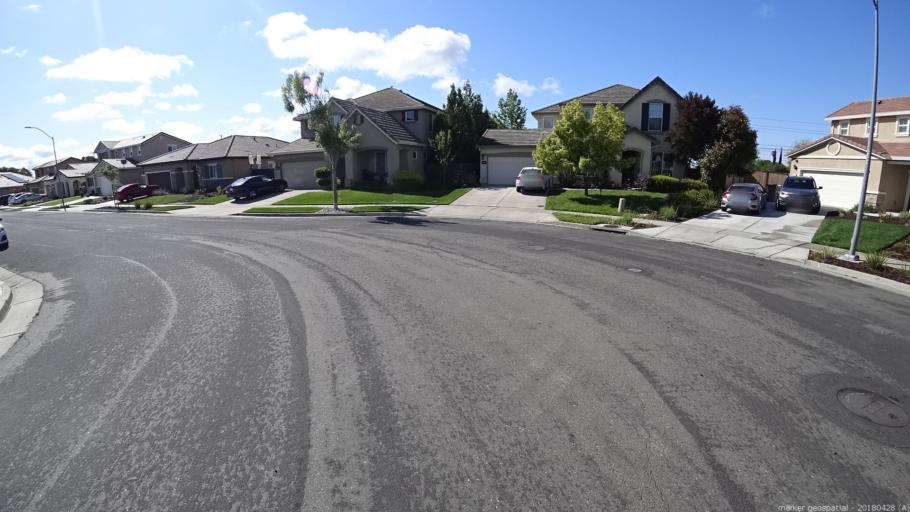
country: US
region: California
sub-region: Yolo County
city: West Sacramento
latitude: 38.5356
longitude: -121.5598
